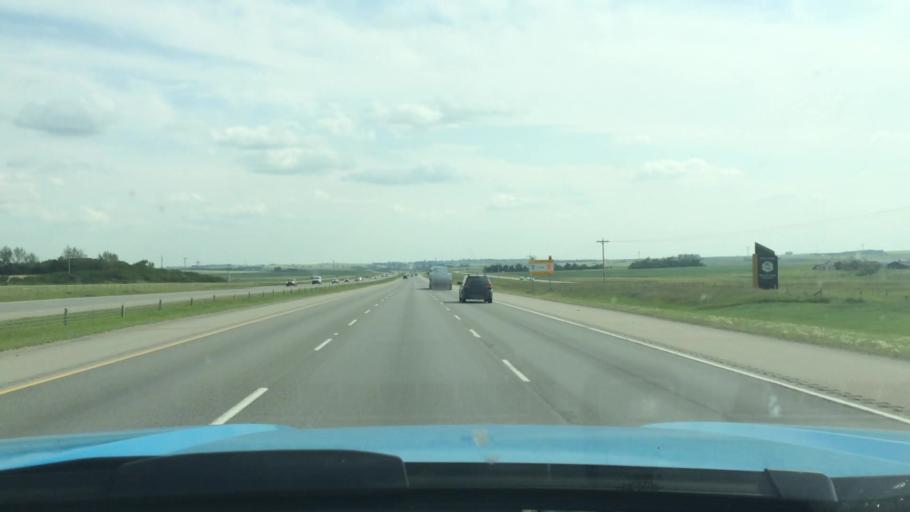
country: CA
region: Alberta
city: Crossfield
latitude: 51.4900
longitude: -114.0253
